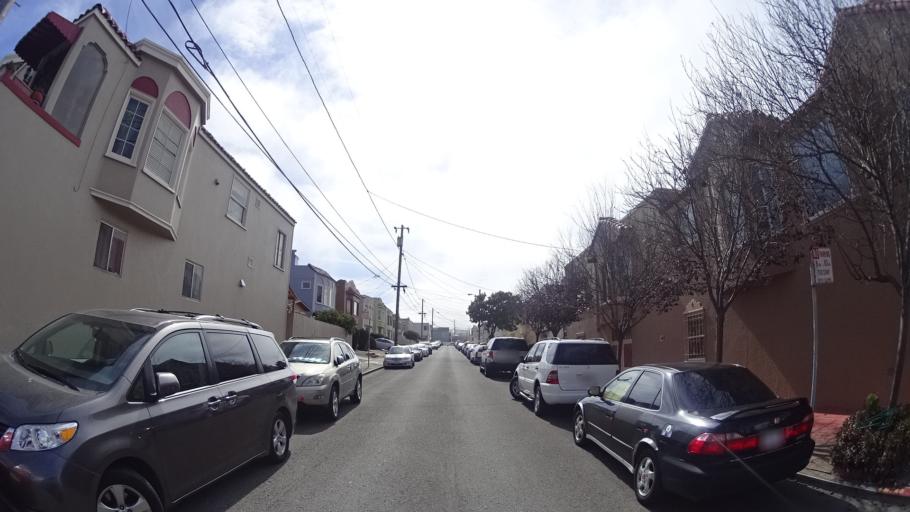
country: US
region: California
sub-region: San Mateo County
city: Daly City
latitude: 37.7126
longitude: -122.4475
